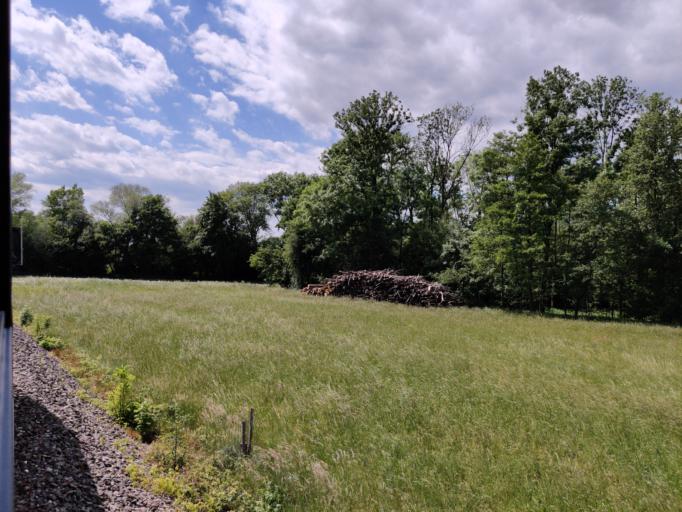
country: SI
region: Apace
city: Apace
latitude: 46.7336
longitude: 15.9107
